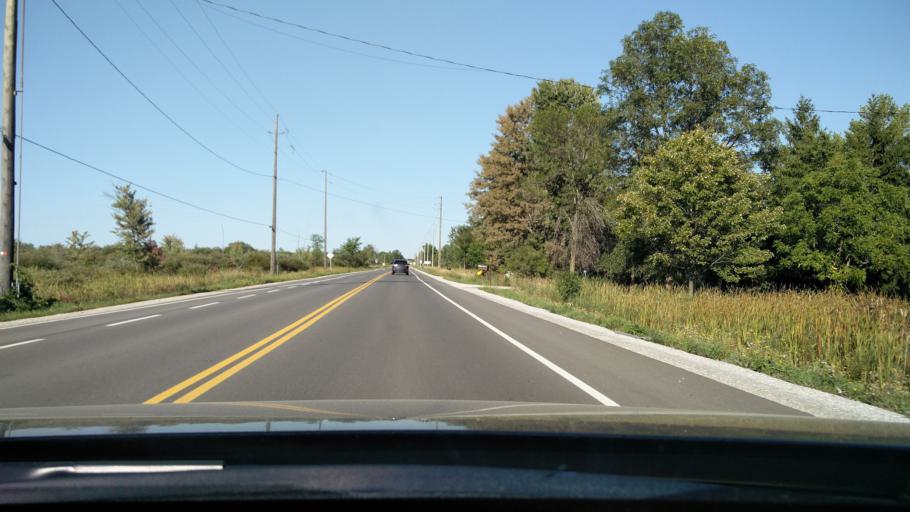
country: CA
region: Ontario
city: Perth
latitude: 44.9073
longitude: -76.2428
